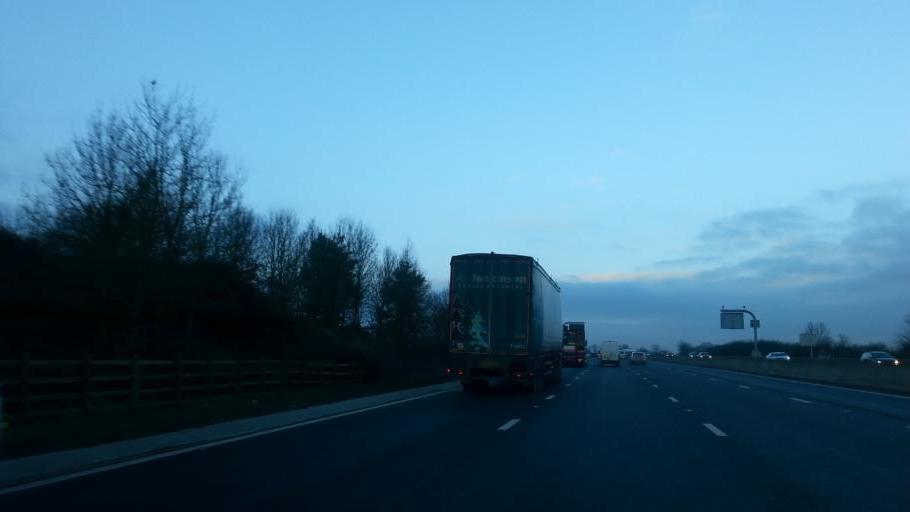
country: GB
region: England
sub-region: Worcestershire
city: Droitwich
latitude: 52.2414
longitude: -2.1346
